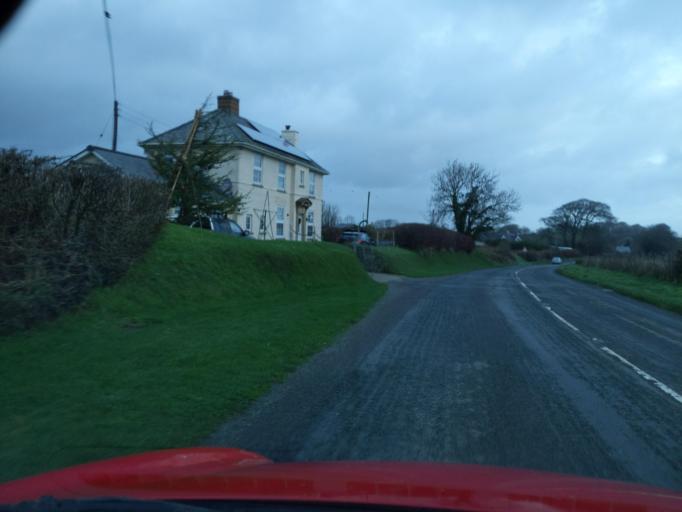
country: GB
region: England
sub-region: Devon
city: Holsworthy
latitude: 50.8795
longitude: -4.3044
